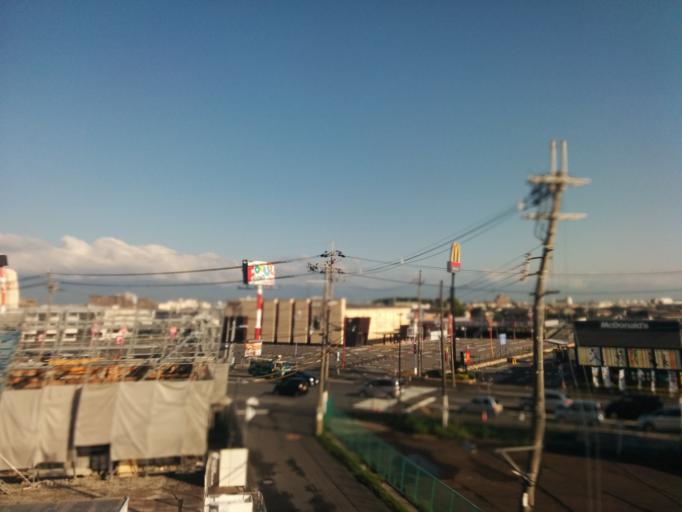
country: JP
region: Shiga Prefecture
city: Kusatsu
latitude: 35.0221
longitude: 135.9822
